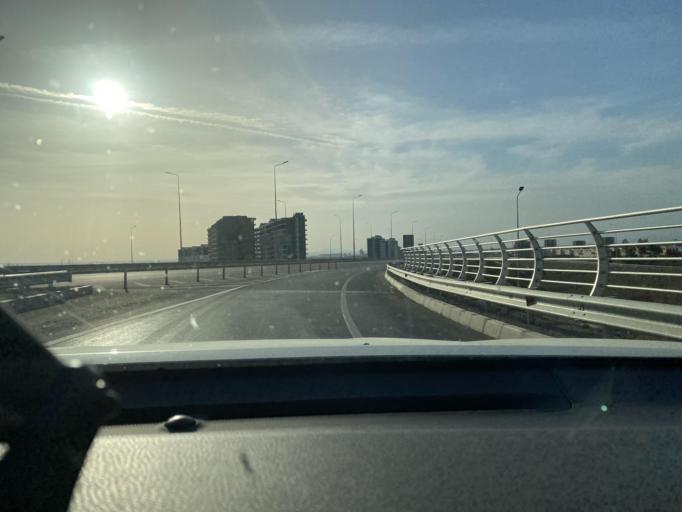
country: IQ
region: Arbil
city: Erbil
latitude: 36.2673
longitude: 44.0916
